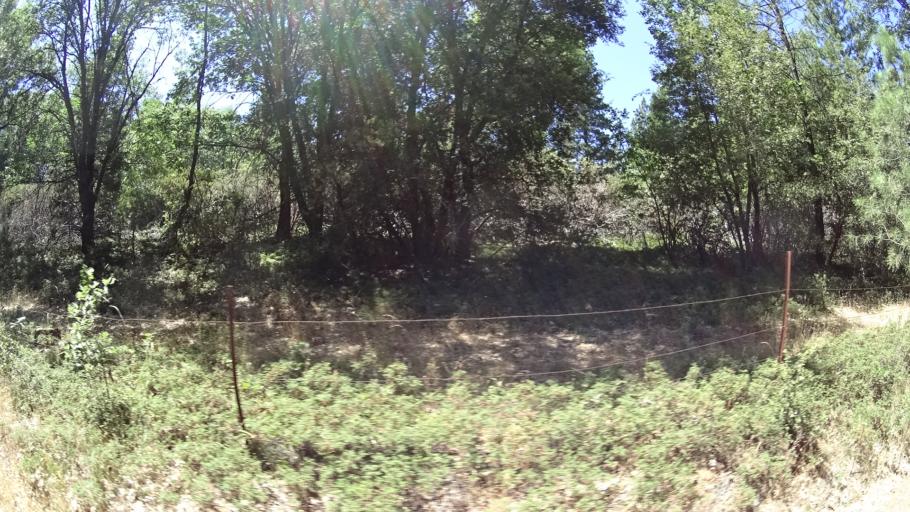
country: US
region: California
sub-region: Calaveras County
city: Mountain Ranch
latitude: 38.3181
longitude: -120.5407
